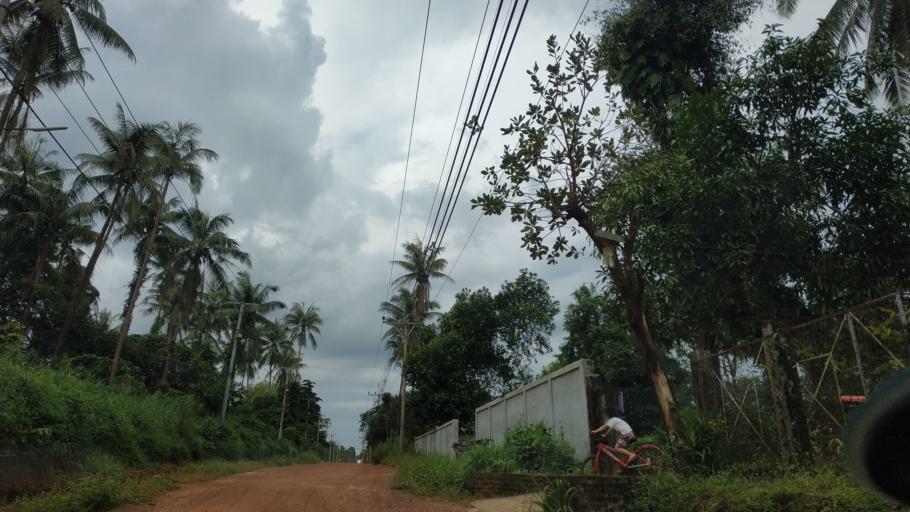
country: MM
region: Tanintharyi
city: Dawei
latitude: 14.0961
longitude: 98.1997
